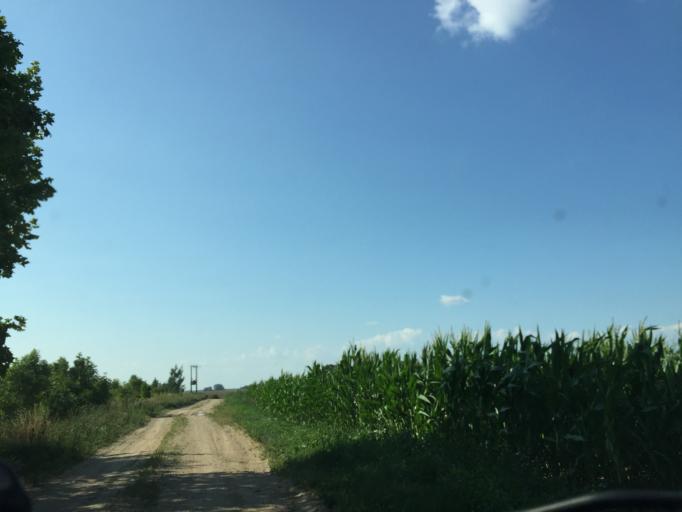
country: LV
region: Jelgava
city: Jelgava
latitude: 56.4696
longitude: 23.6748
